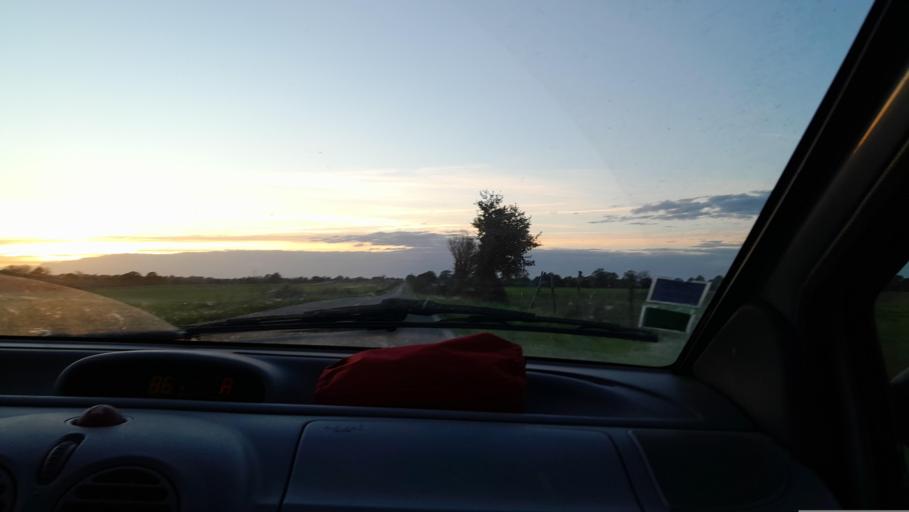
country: FR
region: Pays de la Loire
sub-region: Departement de la Mayenne
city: Ballots
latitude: 47.9017
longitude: -1.1198
